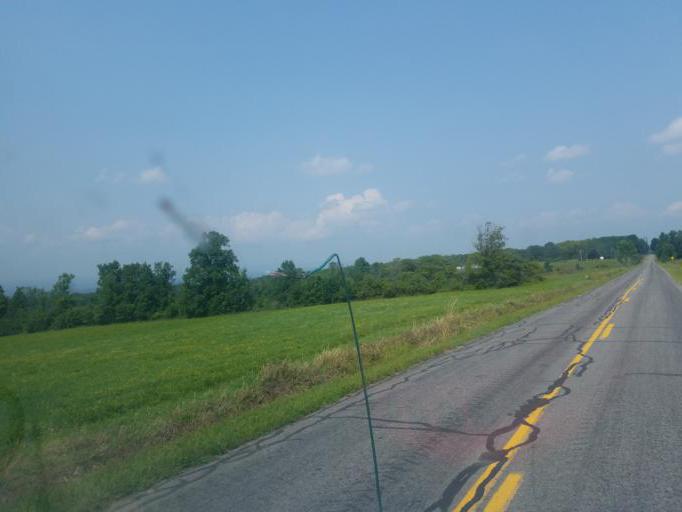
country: US
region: New York
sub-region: Montgomery County
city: Fonda
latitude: 42.8496
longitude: -74.3795
